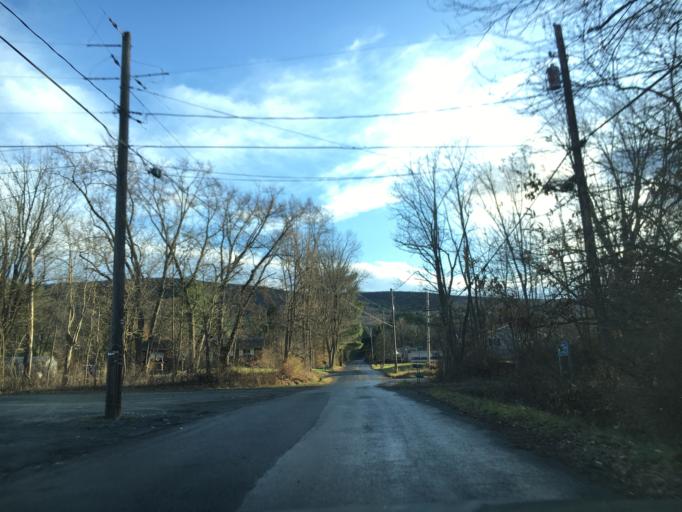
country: US
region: Pennsylvania
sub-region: Carbon County
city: Lehighton
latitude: 40.7794
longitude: -75.7112
